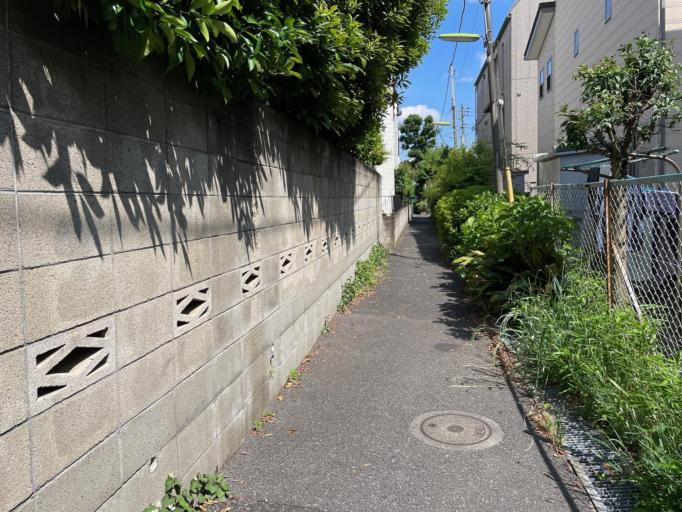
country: JP
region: Tokyo
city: Mitaka-shi
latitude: 35.6646
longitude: 139.6234
